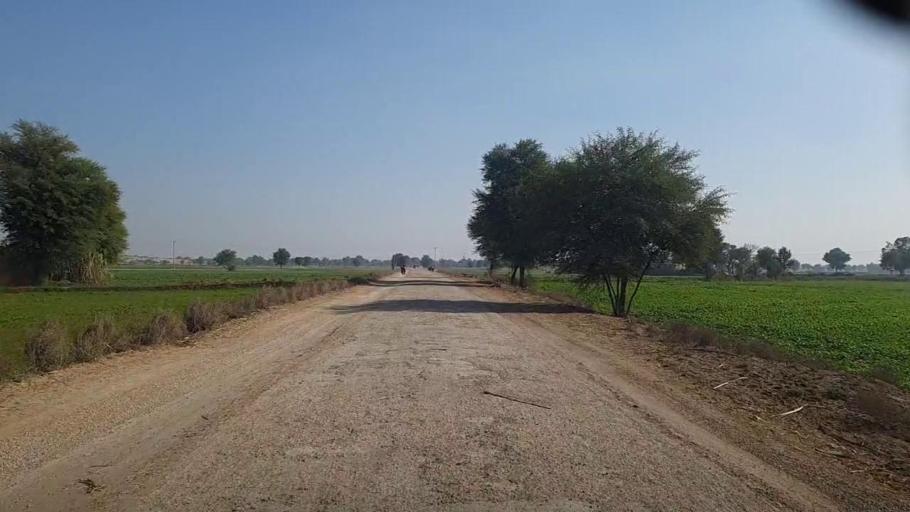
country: PK
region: Sindh
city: Darya Khan Marri
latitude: 26.6686
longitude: 68.3327
